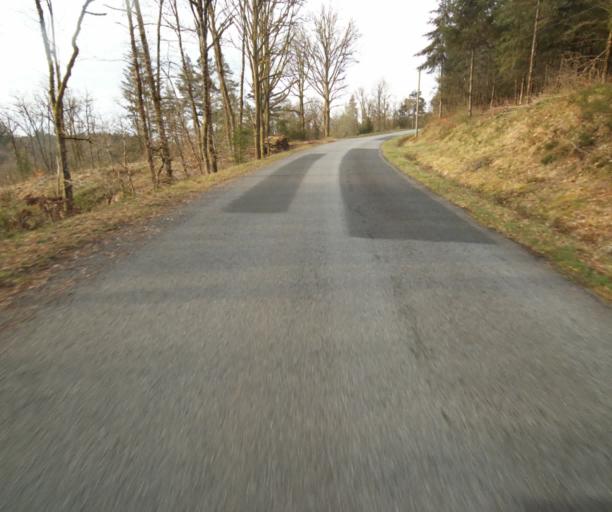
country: FR
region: Limousin
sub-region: Departement de la Correze
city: Correze
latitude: 45.4187
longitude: 1.8940
